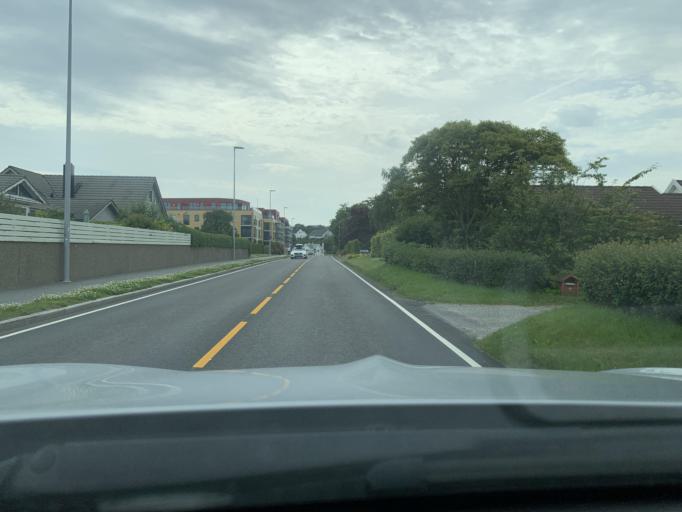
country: NO
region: Rogaland
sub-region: Sandnes
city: Sandnes
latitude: 58.7808
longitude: 5.7188
